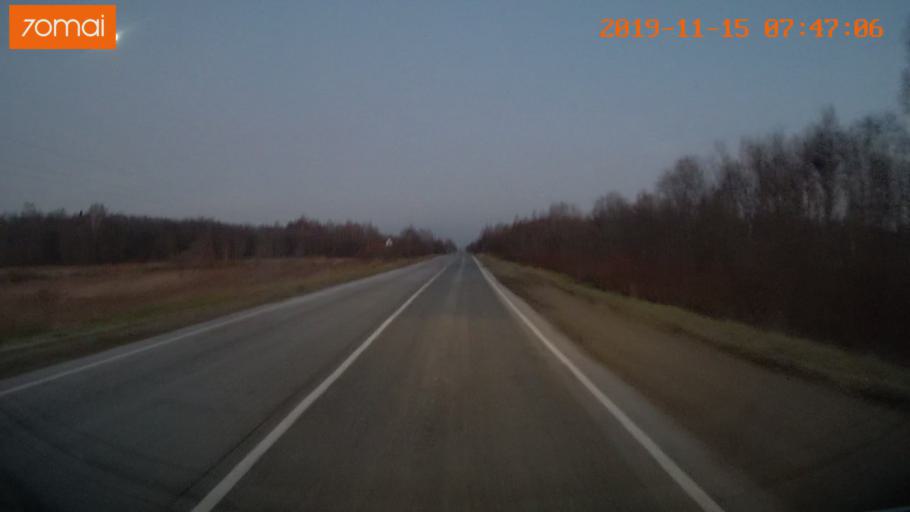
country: RU
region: Vologda
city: Sheksna
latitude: 58.8380
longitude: 38.2677
